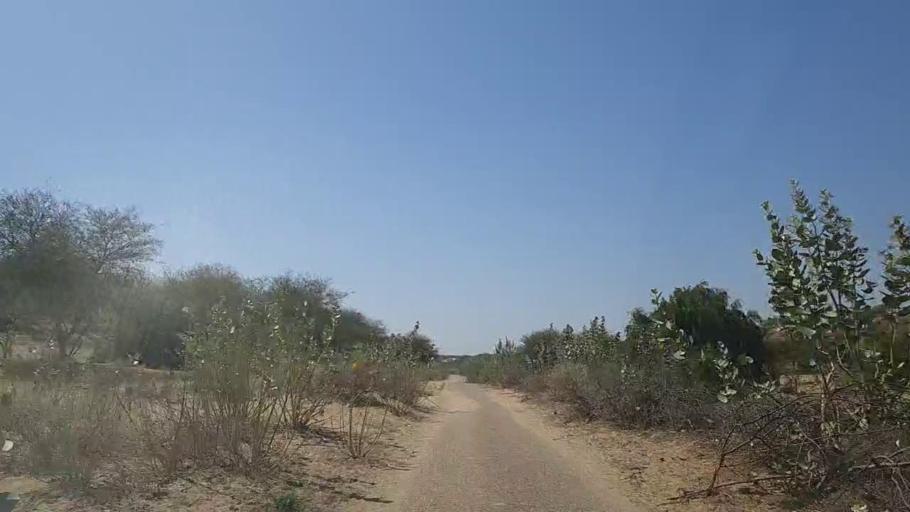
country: PK
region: Sindh
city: Mithi
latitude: 24.8149
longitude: 69.6569
